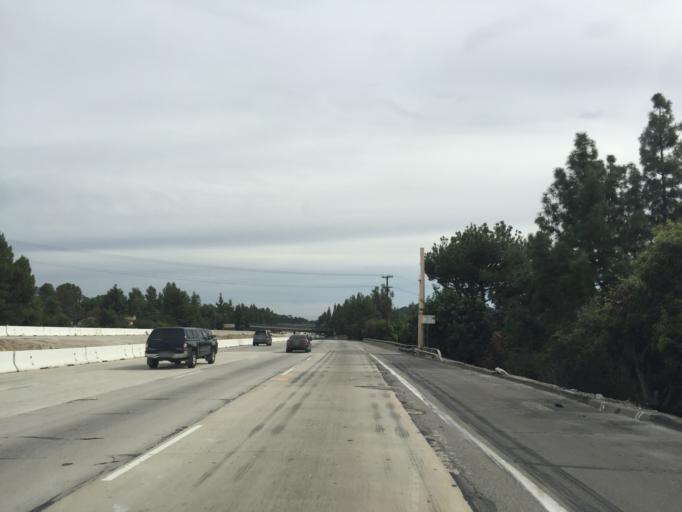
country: US
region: California
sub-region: Los Angeles County
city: La Crescenta-Montrose
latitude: 34.2236
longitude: -118.2498
